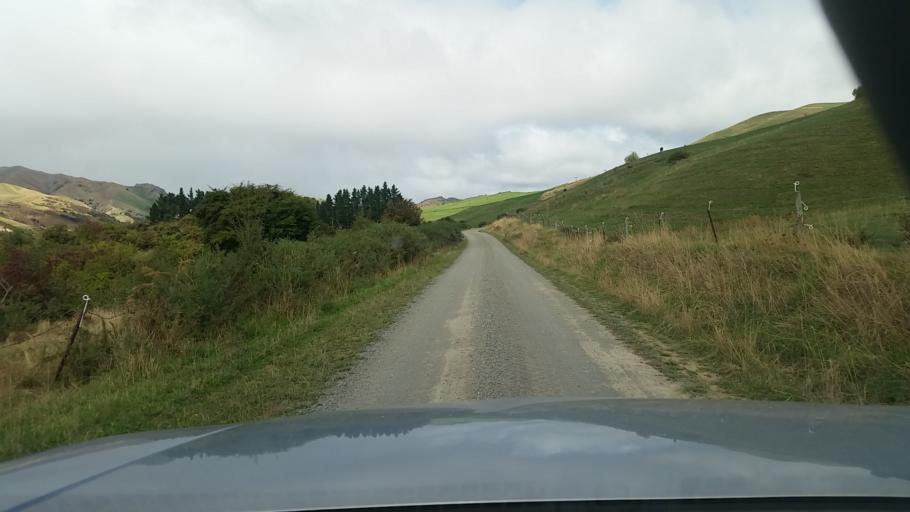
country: NZ
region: Marlborough
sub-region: Marlborough District
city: Blenheim
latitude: -41.7400
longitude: 173.8931
